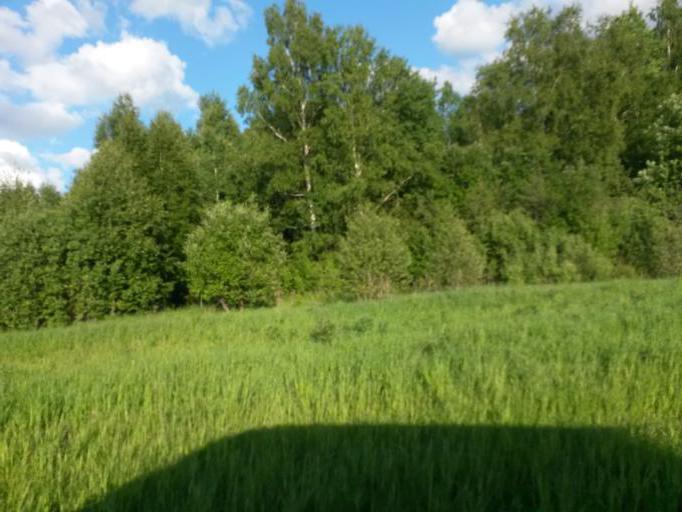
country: RU
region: Jaroslavl
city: Burmakino
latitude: 57.3675
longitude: 40.2015
